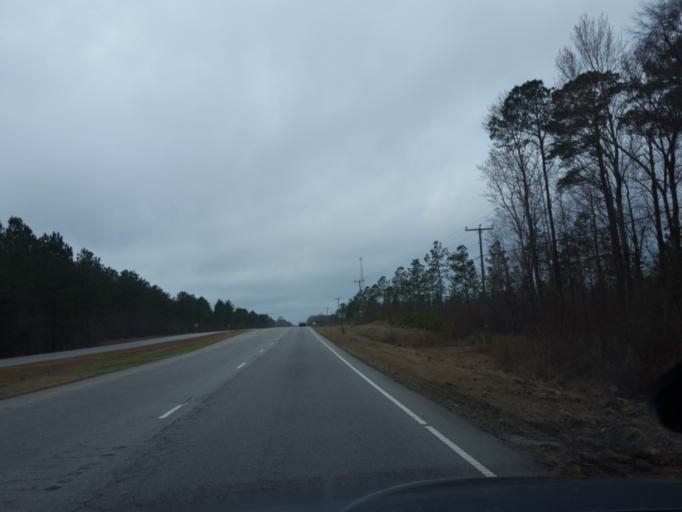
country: US
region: North Carolina
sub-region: Washington County
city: Plymouth
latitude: 35.8121
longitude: -76.8519
